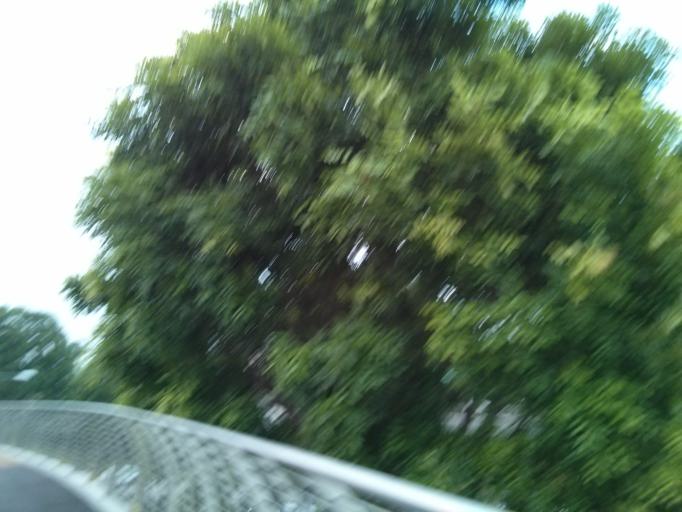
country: SG
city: Singapore
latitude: 1.3217
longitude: 103.7514
